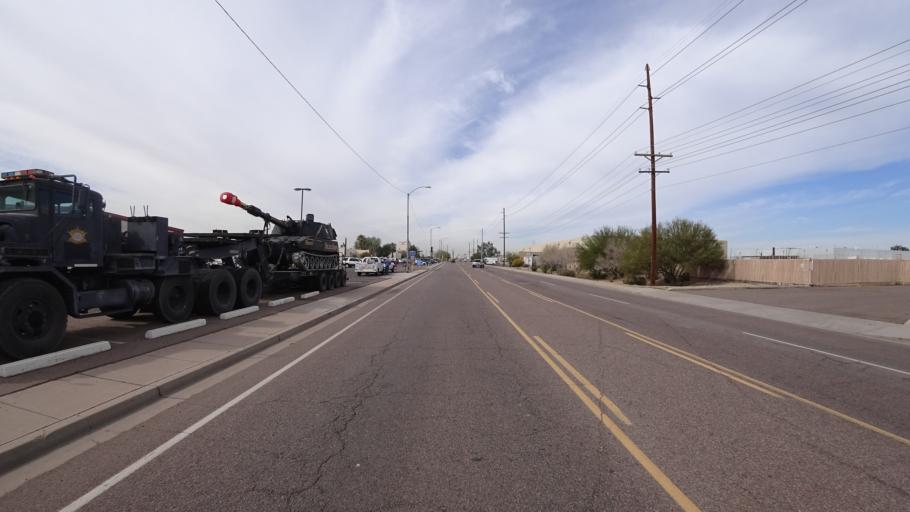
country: US
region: Arizona
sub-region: Maricopa County
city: Phoenix
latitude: 33.4296
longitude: -112.1305
